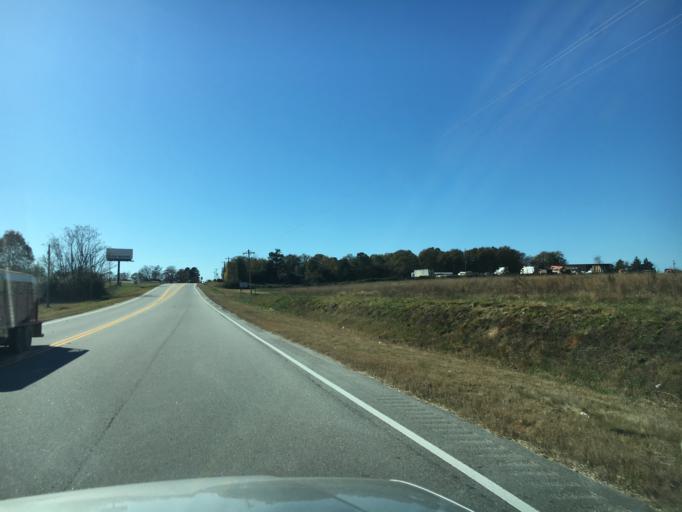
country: US
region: Georgia
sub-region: Hart County
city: Royston
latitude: 34.2934
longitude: -83.0401
